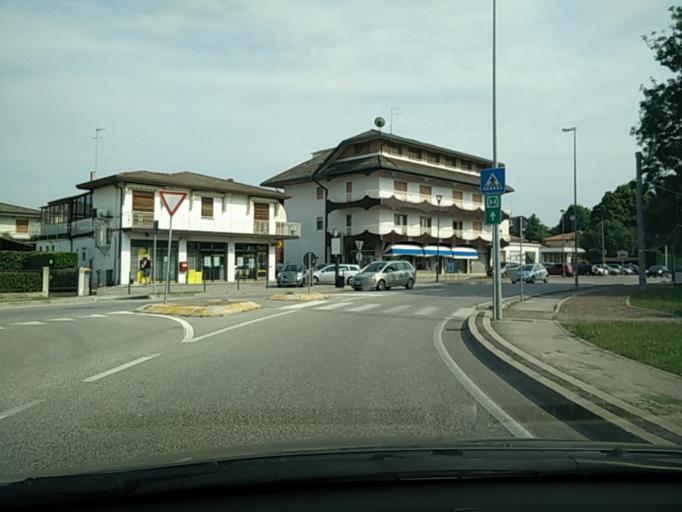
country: IT
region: Veneto
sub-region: Provincia di Treviso
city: Casale sul Sile
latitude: 45.5996
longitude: 12.3258
